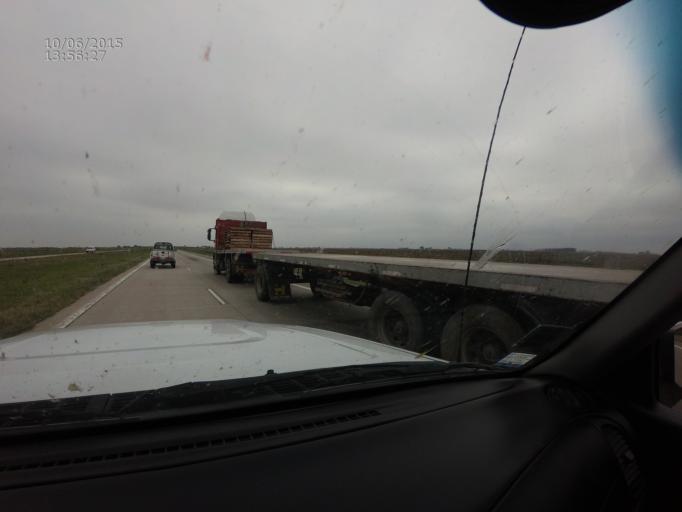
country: AR
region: Cordoba
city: Morrison
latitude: -32.5644
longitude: -62.8098
